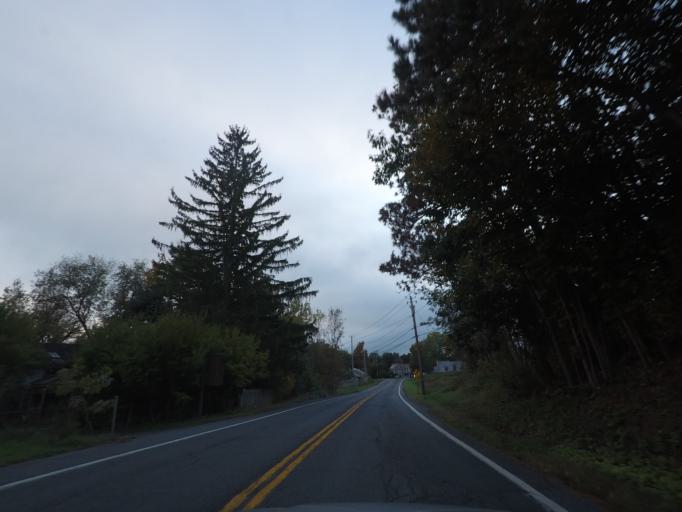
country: US
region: New York
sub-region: Rensselaer County
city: Nassau
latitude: 42.5627
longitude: -73.6316
